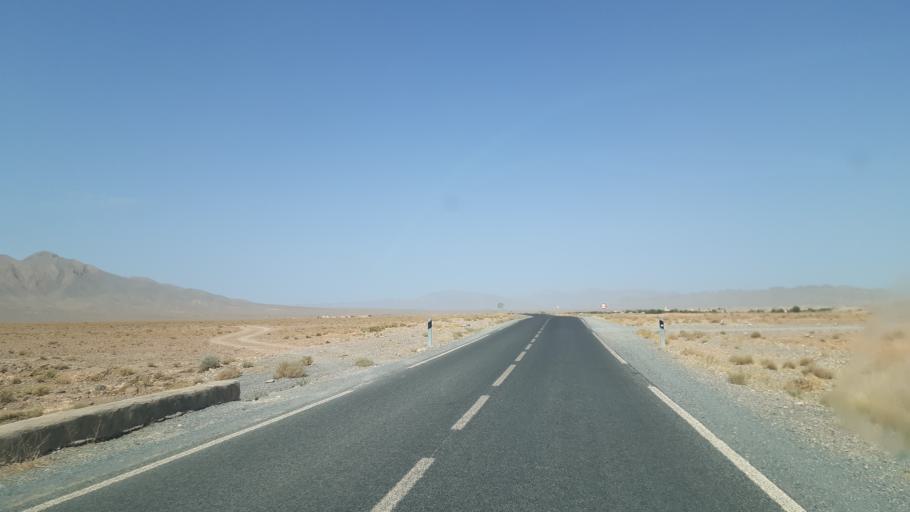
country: MA
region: Meknes-Tafilalet
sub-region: Errachidia
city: Amouguer
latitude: 32.2301
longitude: -4.6587
